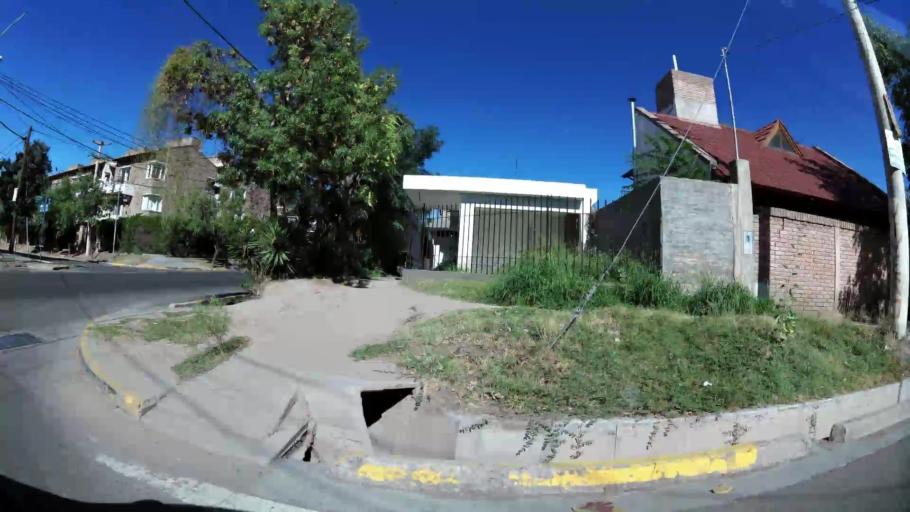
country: AR
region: Mendoza
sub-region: Departamento de Godoy Cruz
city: Godoy Cruz
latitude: -32.9317
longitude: -68.8619
